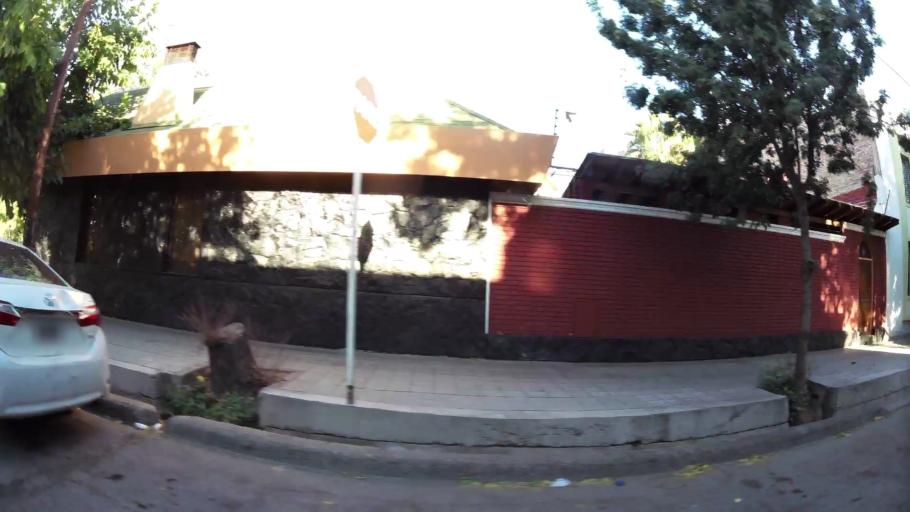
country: AR
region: Mendoza
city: Mendoza
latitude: -32.8777
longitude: -68.8295
